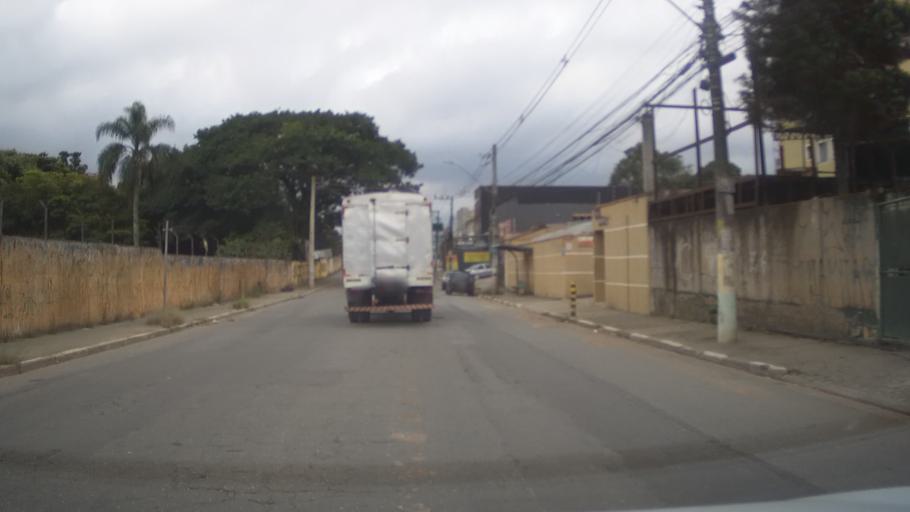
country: BR
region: Sao Paulo
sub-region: Aruja
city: Aruja
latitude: -23.4045
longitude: -46.4067
